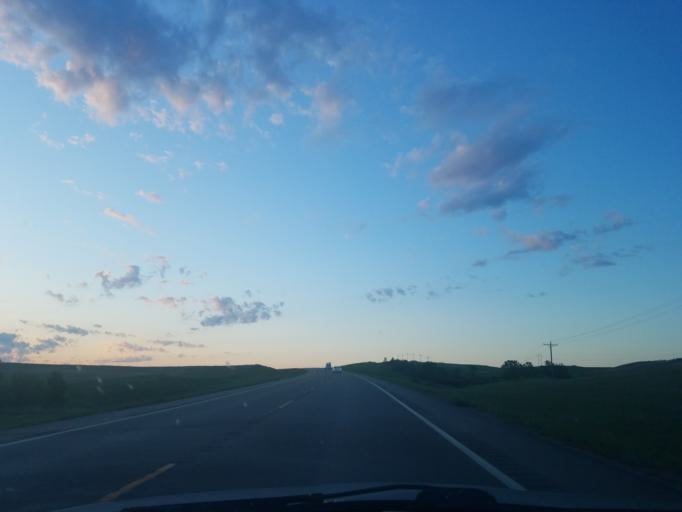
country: US
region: North Dakota
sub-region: McKenzie County
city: Watford City
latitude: 47.6469
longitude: -103.2699
